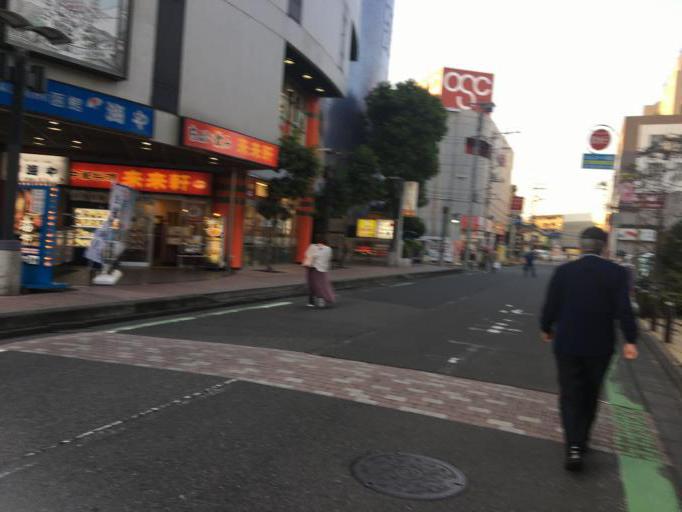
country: JP
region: Saitama
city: Shiki
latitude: 35.8156
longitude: 139.5866
